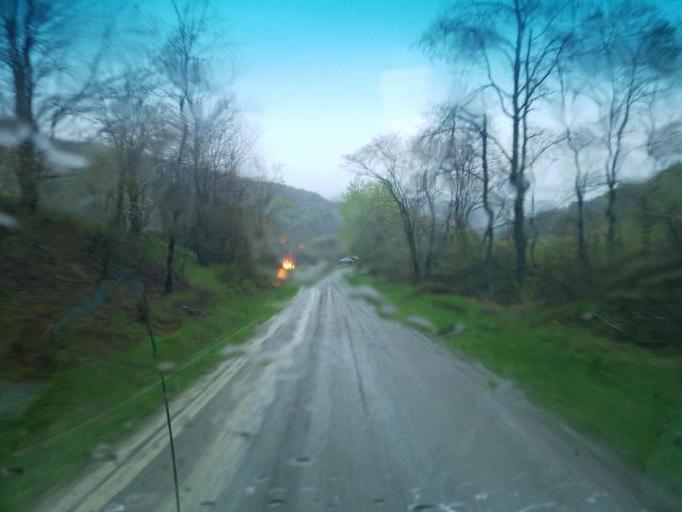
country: US
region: Pennsylvania
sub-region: Tioga County
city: Westfield
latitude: 41.9015
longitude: -77.7169
